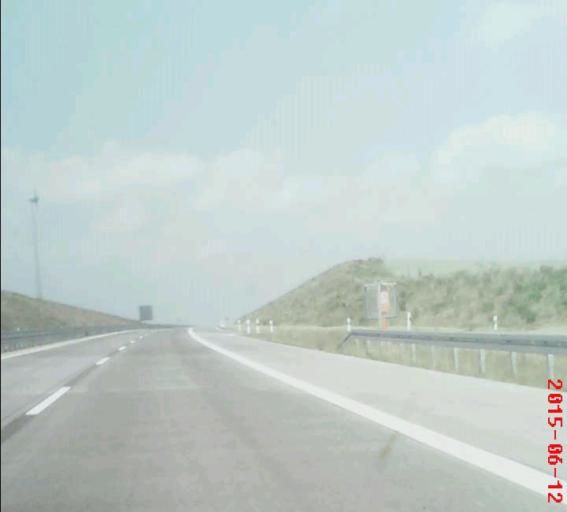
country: DE
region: Thuringia
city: Artern
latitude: 51.3817
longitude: 11.2761
